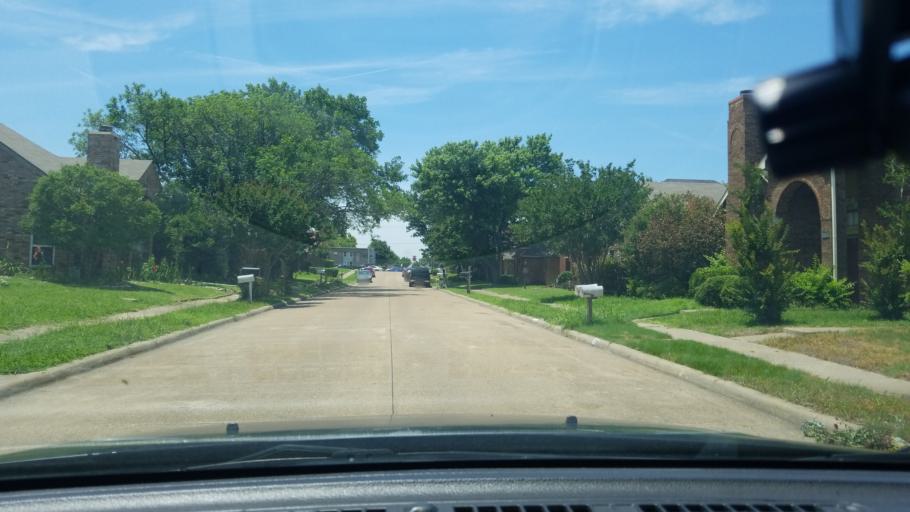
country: US
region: Texas
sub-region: Dallas County
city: Mesquite
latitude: 32.7887
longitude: -96.6011
